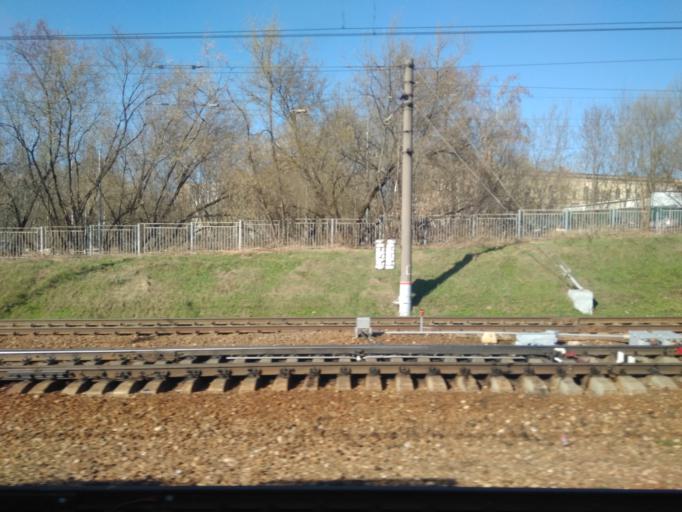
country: RU
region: Moscow
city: Strogino
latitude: 55.8293
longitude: 37.4303
